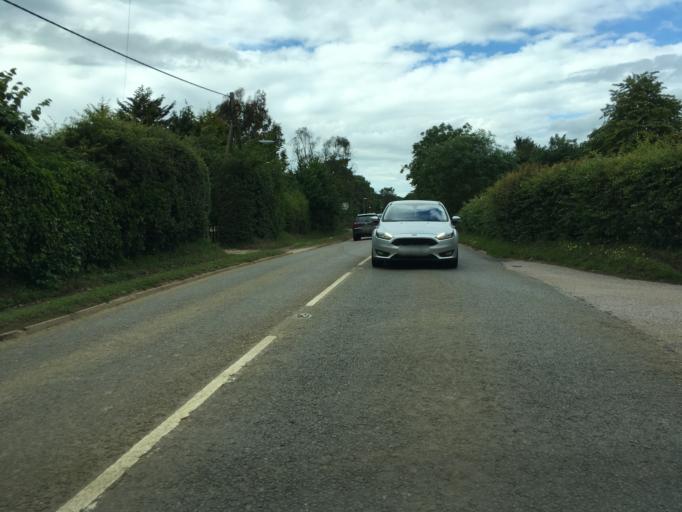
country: GB
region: England
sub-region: Central Bedfordshire
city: Leighton Buzzard
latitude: 51.9499
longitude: -0.6551
